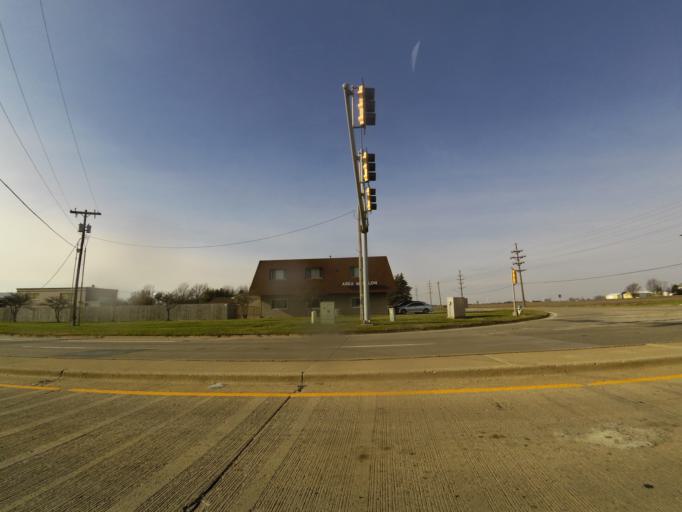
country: US
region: Illinois
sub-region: Macon County
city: Forsyth
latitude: 39.9348
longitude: -88.9556
